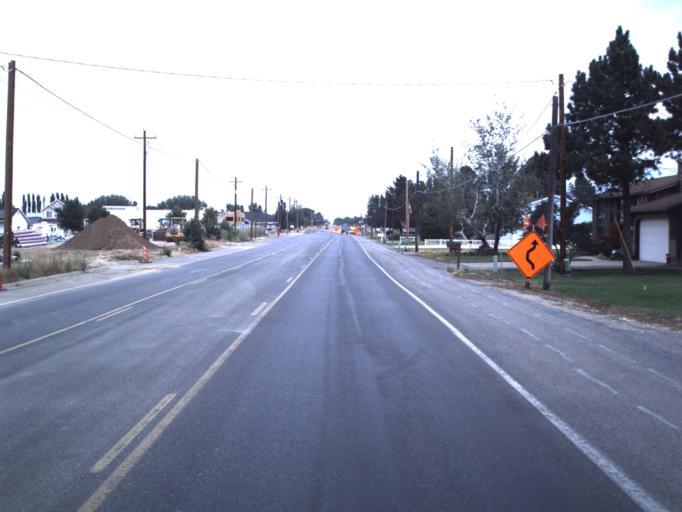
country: US
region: Utah
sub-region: Davis County
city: Syracuse
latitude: 41.0972
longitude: -112.0646
